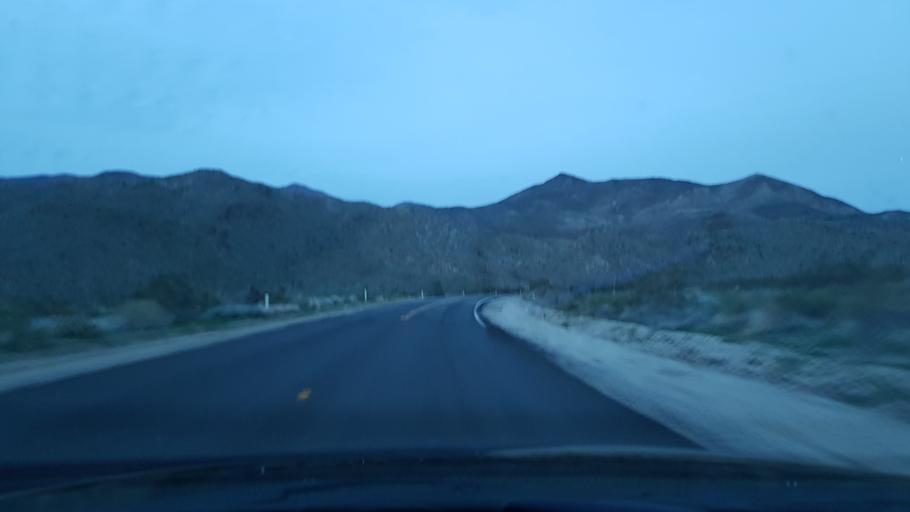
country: US
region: California
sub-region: San Diego County
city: Julian
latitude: 33.0077
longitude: -116.4563
